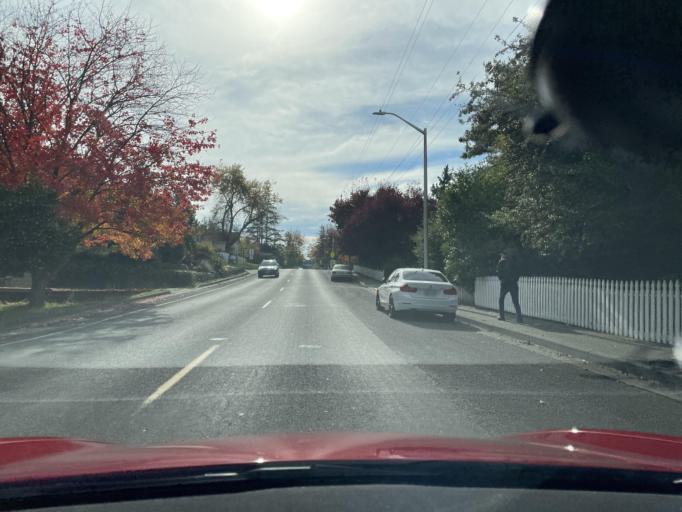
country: US
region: Washington
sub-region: San Juan County
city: Friday Harbor
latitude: 48.5304
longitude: -123.0176
